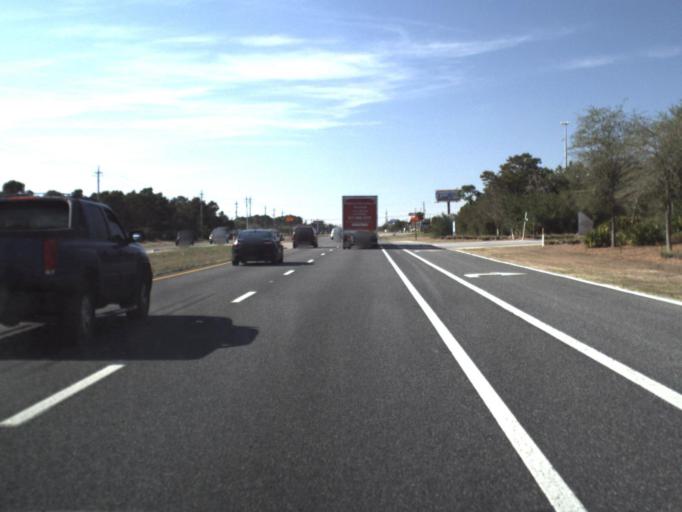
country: US
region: Florida
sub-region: Bay County
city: Laguna Beach
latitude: 30.2365
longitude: -85.9047
